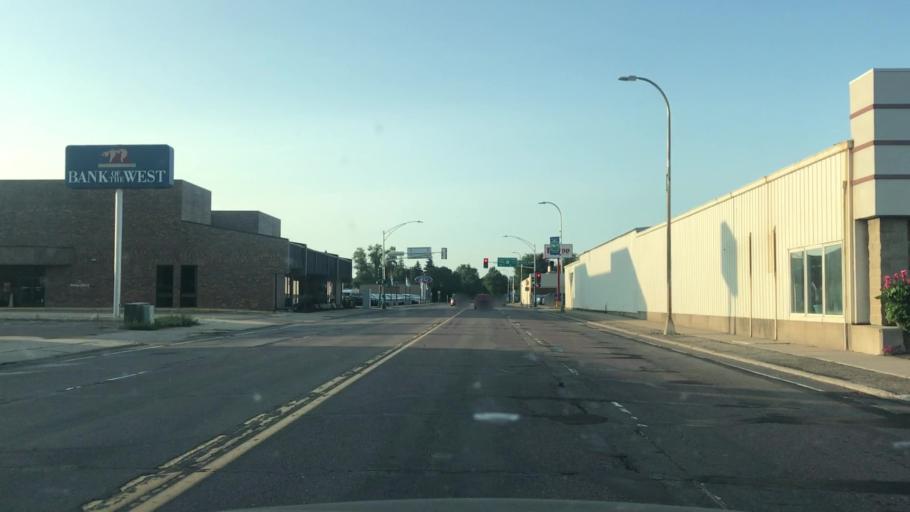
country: US
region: Minnesota
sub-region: Cottonwood County
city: Windom
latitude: 43.8656
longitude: -95.1149
